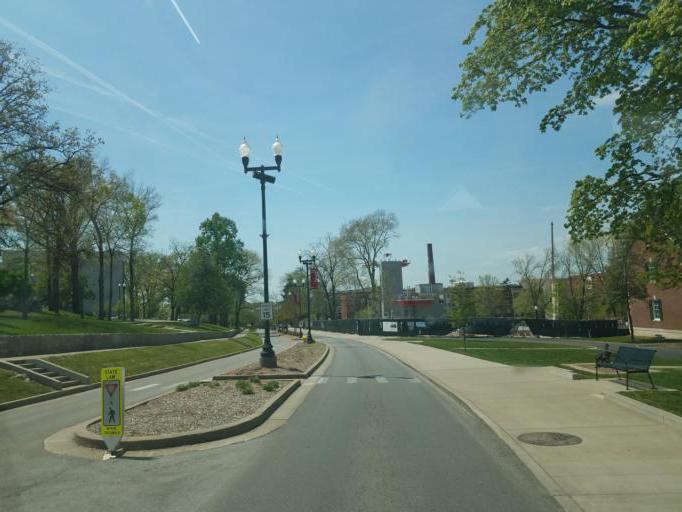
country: US
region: Kentucky
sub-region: Warren County
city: Bowling Green
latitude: 36.9887
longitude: -86.4537
